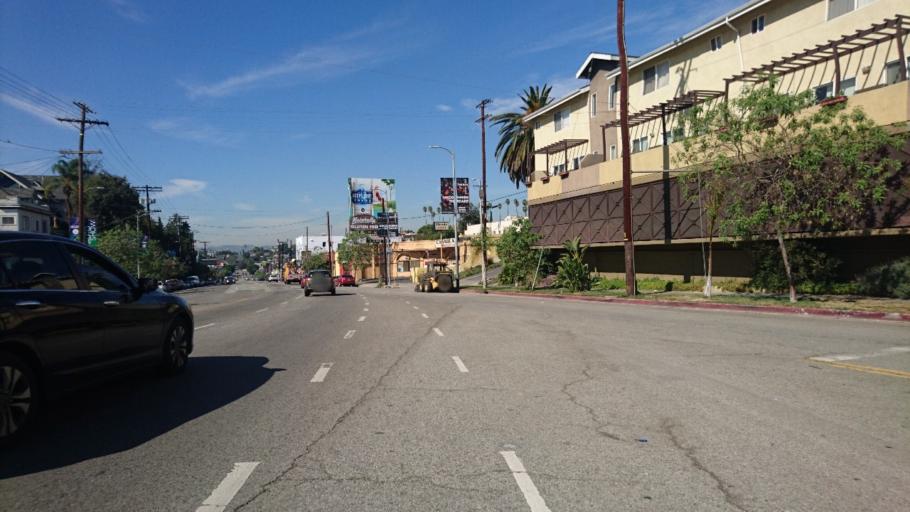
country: US
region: California
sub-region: Los Angeles County
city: Echo Park
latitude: 34.0745
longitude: -118.2521
